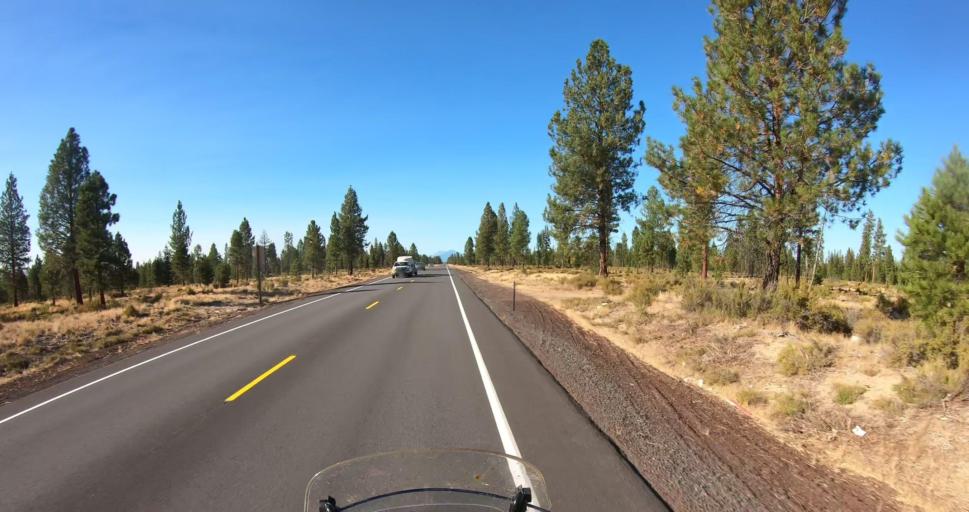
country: US
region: Oregon
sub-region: Deschutes County
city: La Pine
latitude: 43.5444
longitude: -121.4682
